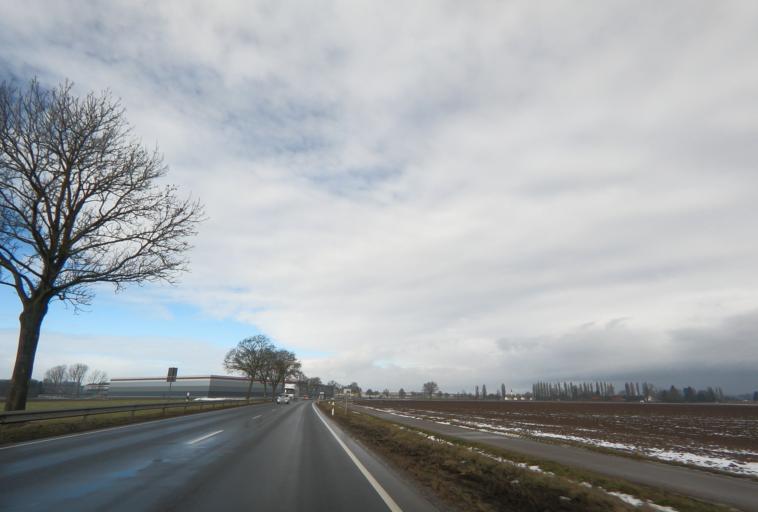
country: DE
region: Bavaria
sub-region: Upper Palatinate
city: Obertraubling
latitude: 48.9505
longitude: 12.1814
